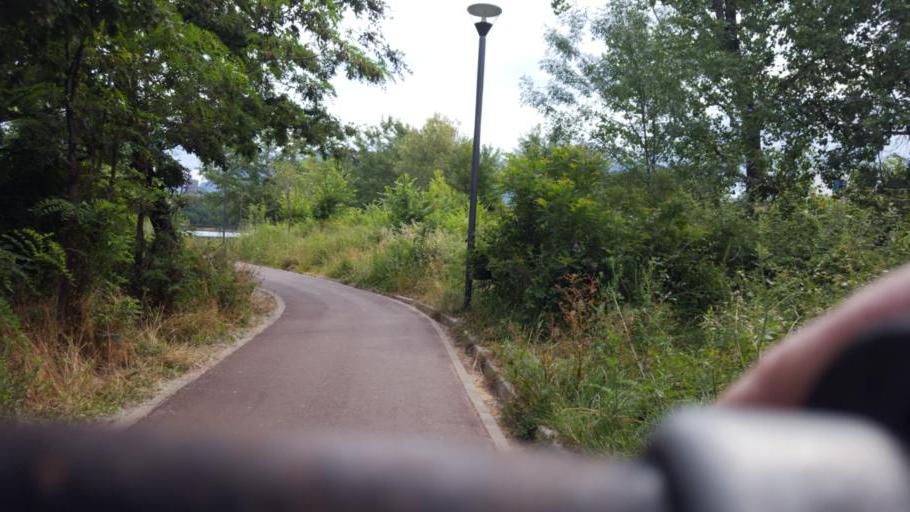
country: AL
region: Tirane
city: Tirana
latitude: 41.3082
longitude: 19.8126
